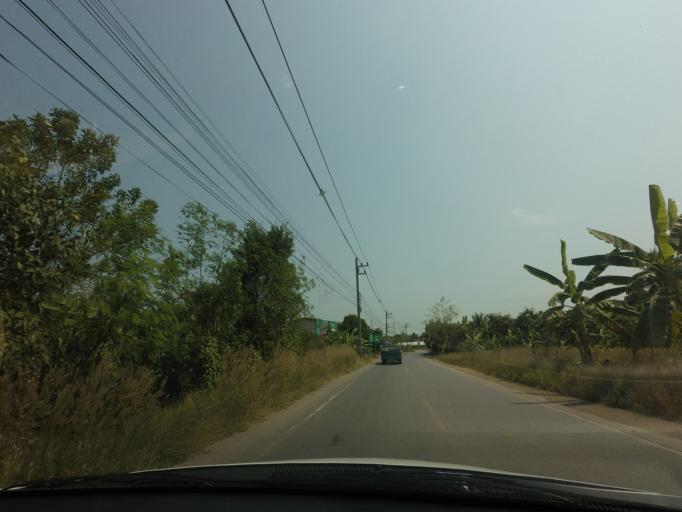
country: TH
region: Nakhon Pathom
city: Sam Phran
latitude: 13.7646
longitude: 100.2439
